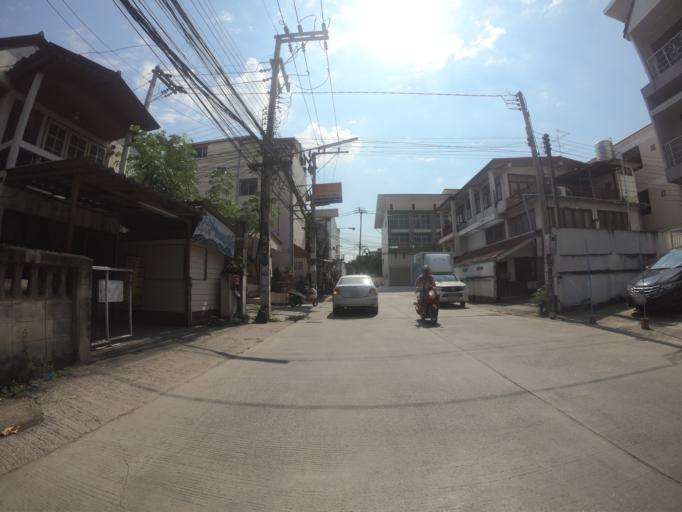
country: TH
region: Chiang Mai
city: Chiang Mai
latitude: 18.8056
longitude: 98.9930
